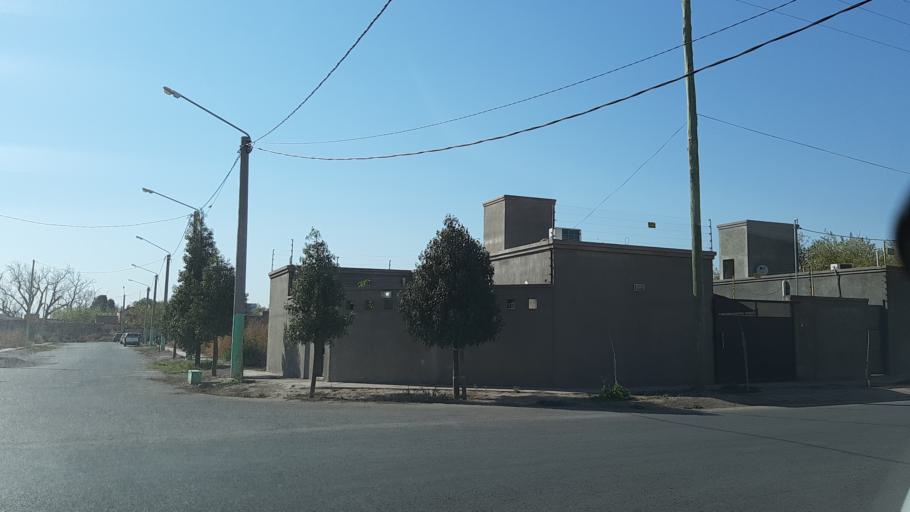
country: AR
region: San Juan
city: San Juan
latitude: -31.5231
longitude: -68.5822
